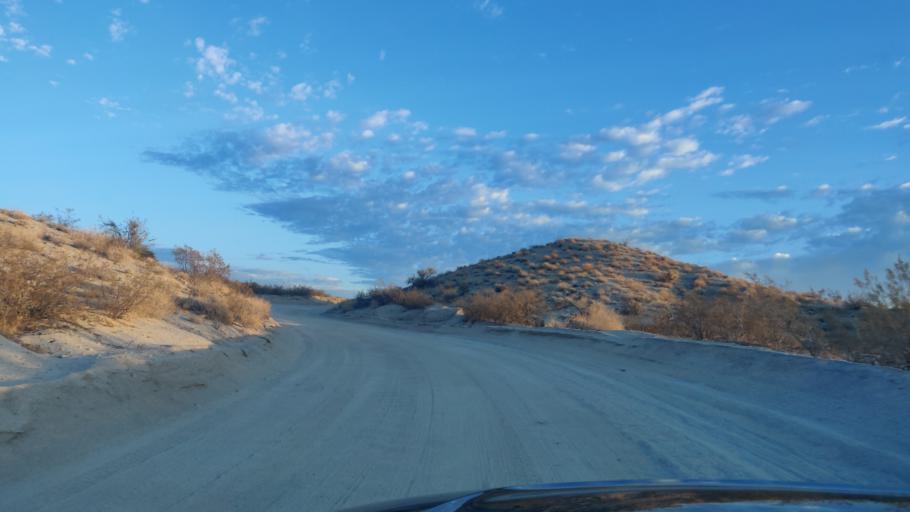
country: US
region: Nevada
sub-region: Clark County
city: Laughlin
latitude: 35.2135
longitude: -114.6749
